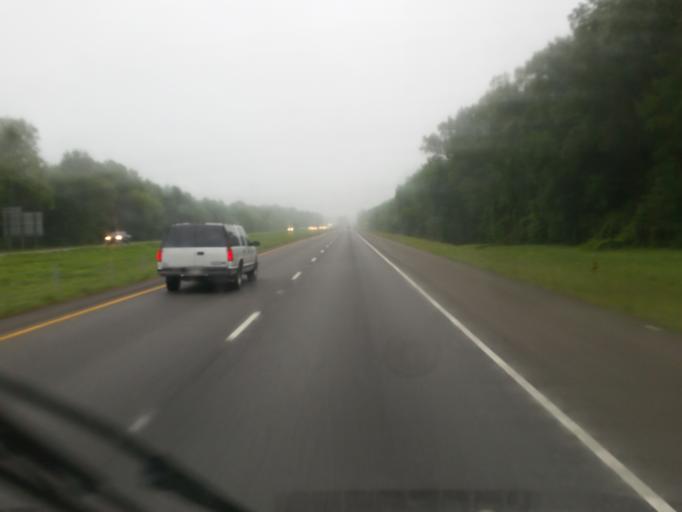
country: US
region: Louisiana
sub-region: Bossier Parish
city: Eastwood
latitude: 32.5419
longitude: -93.5884
